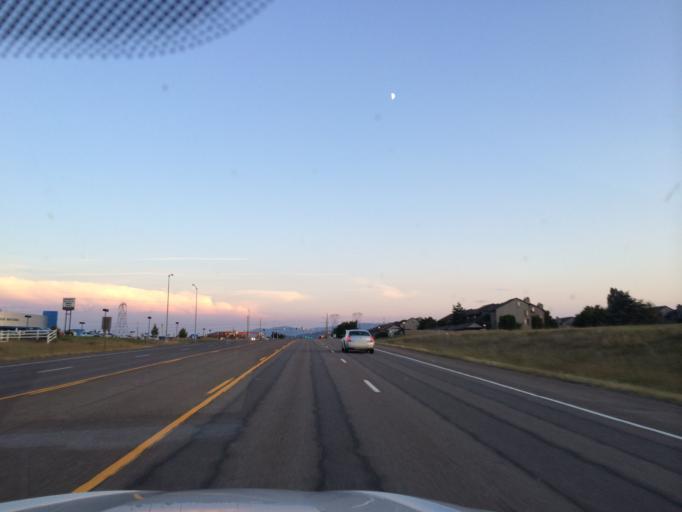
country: US
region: Montana
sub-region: Flathead County
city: Kalispell
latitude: 48.2443
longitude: -114.3306
